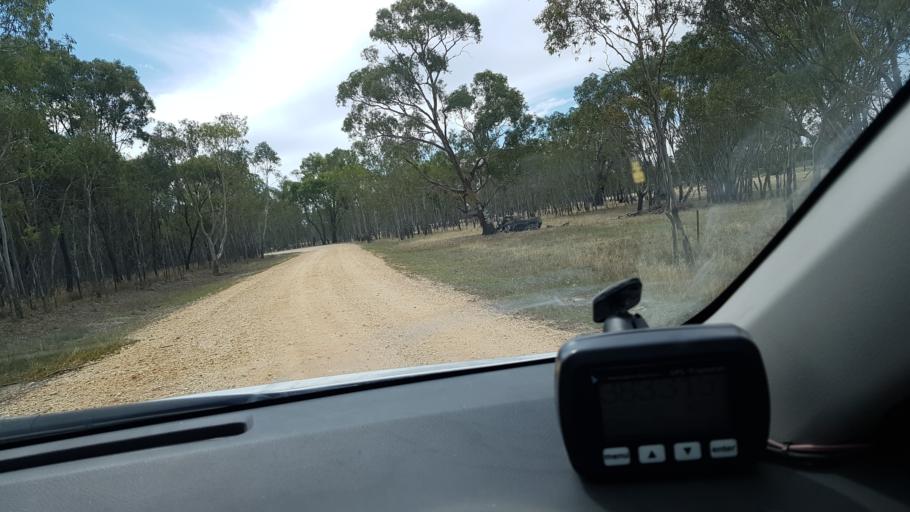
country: AU
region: Victoria
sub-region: Horsham
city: Horsham
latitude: -36.6863
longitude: 141.7795
